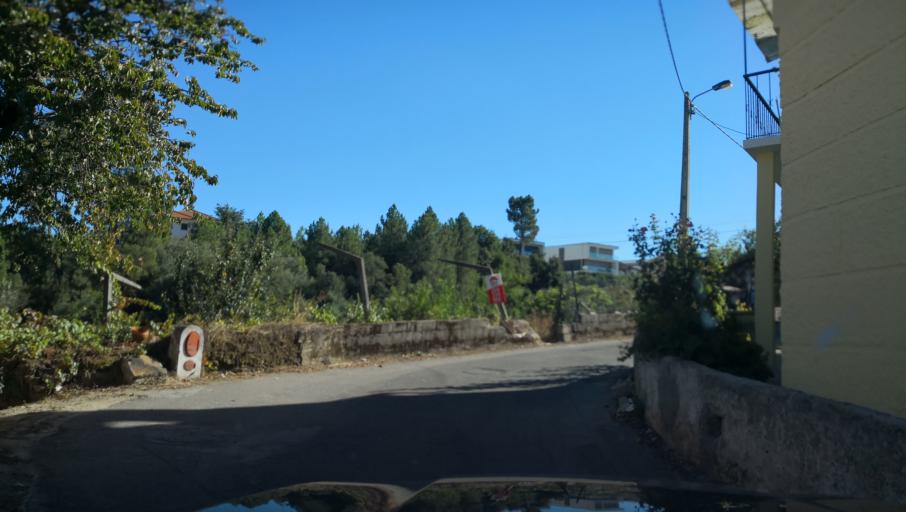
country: PT
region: Vila Real
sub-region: Vila Real
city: Vila Real
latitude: 41.2851
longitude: -7.7210
